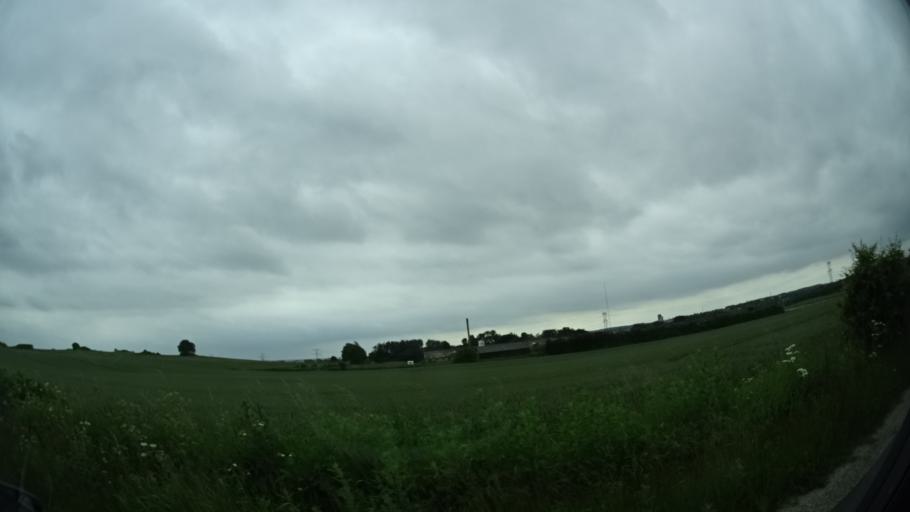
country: DK
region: Central Jutland
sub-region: Arhus Kommune
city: Kolt
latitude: 56.0994
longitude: 10.0642
